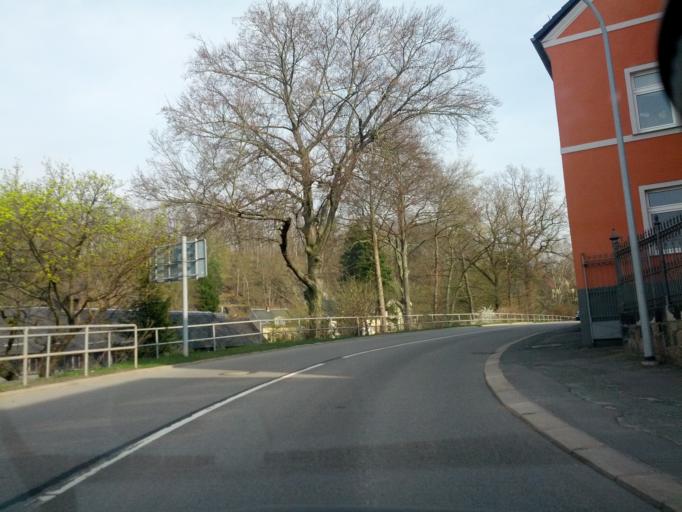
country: DE
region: Saxony
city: Kirchberg
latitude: 50.6218
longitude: 12.5321
